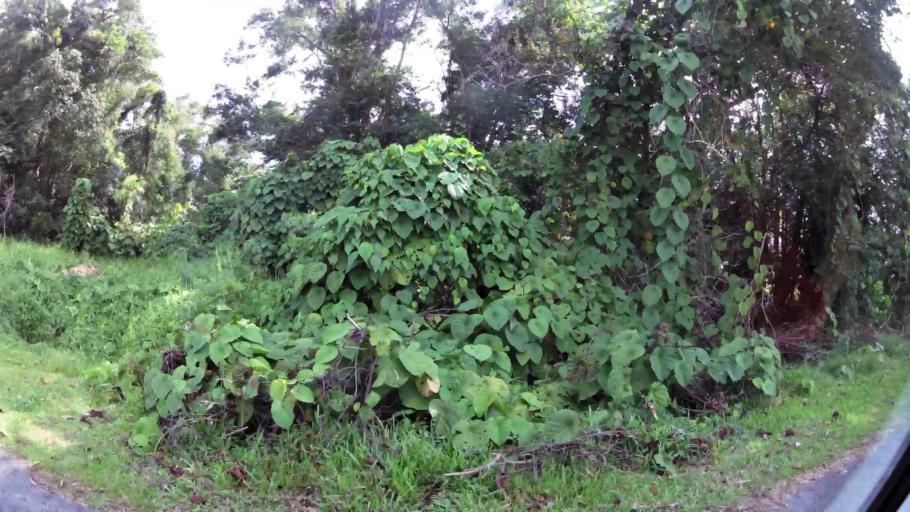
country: BN
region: Brunei and Muara
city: Bandar Seri Begawan
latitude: 4.9530
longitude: 114.9676
